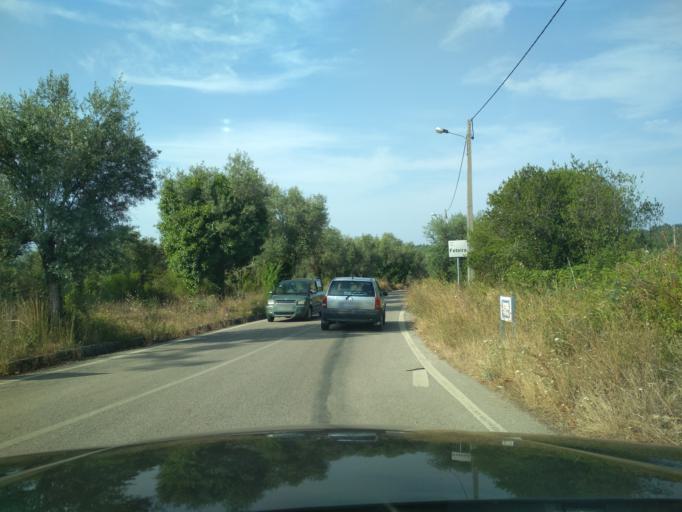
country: PT
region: Coimbra
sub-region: Condeixa-A-Nova
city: Condeixa-a-Nova
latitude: 40.1345
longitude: -8.4598
